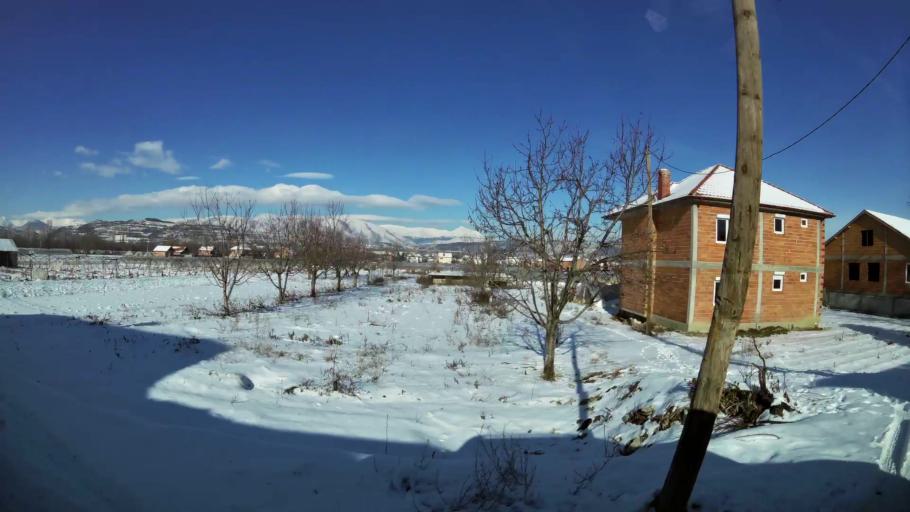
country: MK
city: Grchec
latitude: 41.9866
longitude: 21.3293
